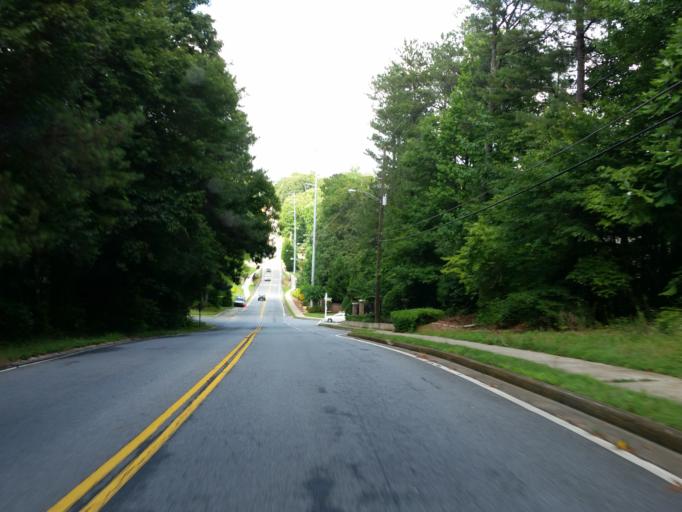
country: US
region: Georgia
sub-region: Fulton County
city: Roswell
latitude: 34.0406
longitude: -84.4238
